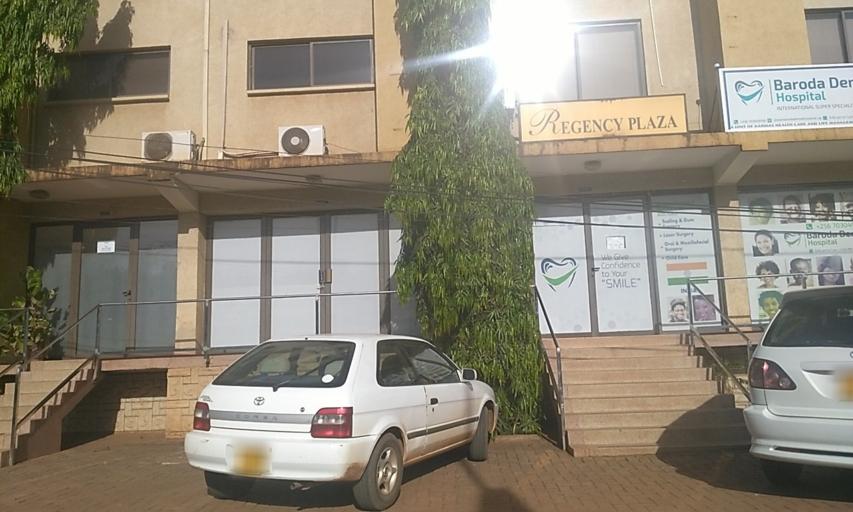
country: UG
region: Central Region
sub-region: Kampala District
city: Kampala
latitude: 0.3312
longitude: 32.6025
